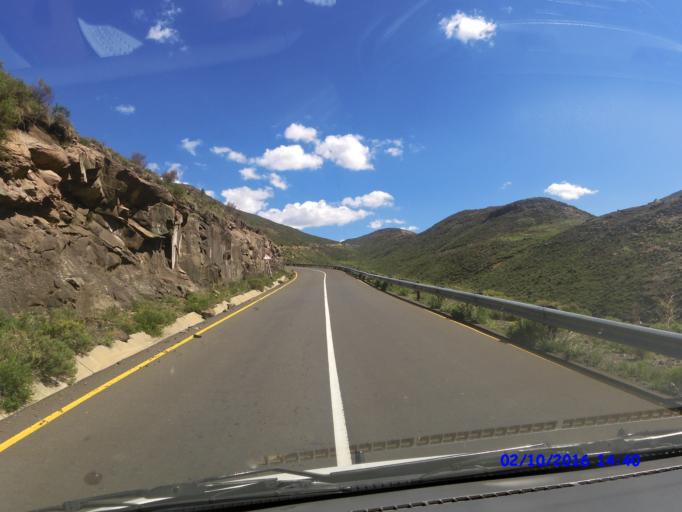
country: LS
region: Maseru
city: Nako
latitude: -29.5213
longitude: 28.0612
